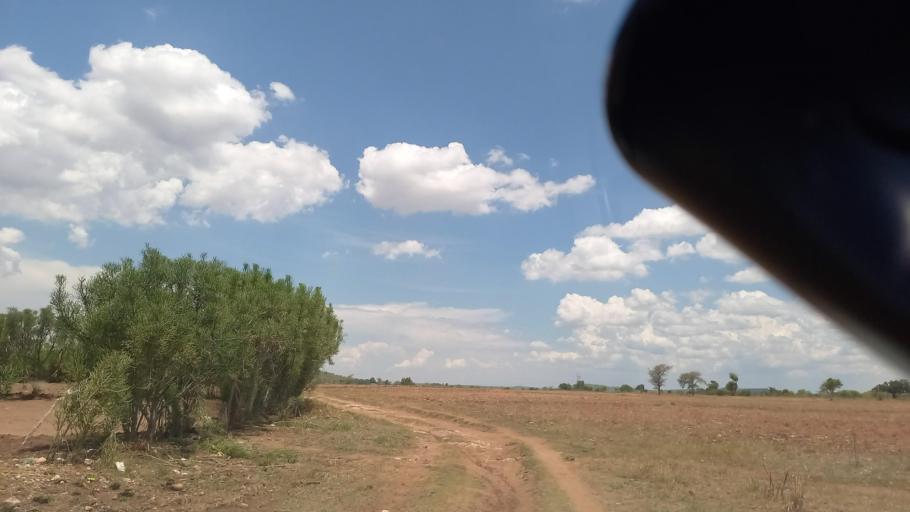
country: ZM
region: Southern
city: Mazabuka
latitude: -16.1101
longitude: 27.8252
